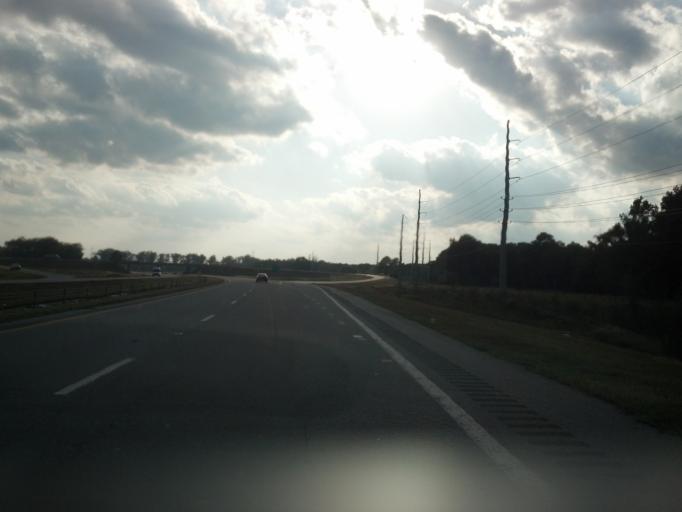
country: US
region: North Carolina
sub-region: Pitt County
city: Greenville
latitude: 35.6636
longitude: -77.4070
